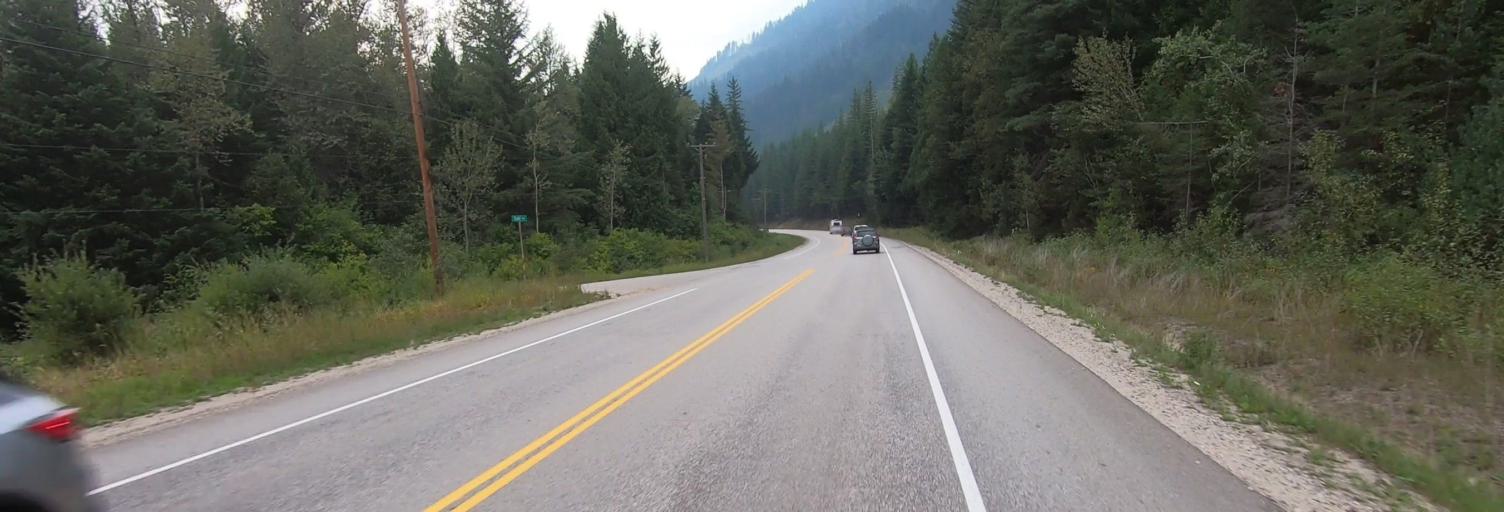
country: CA
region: British Columbia
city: Sicamous
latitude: 51.0005
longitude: -118.6517
